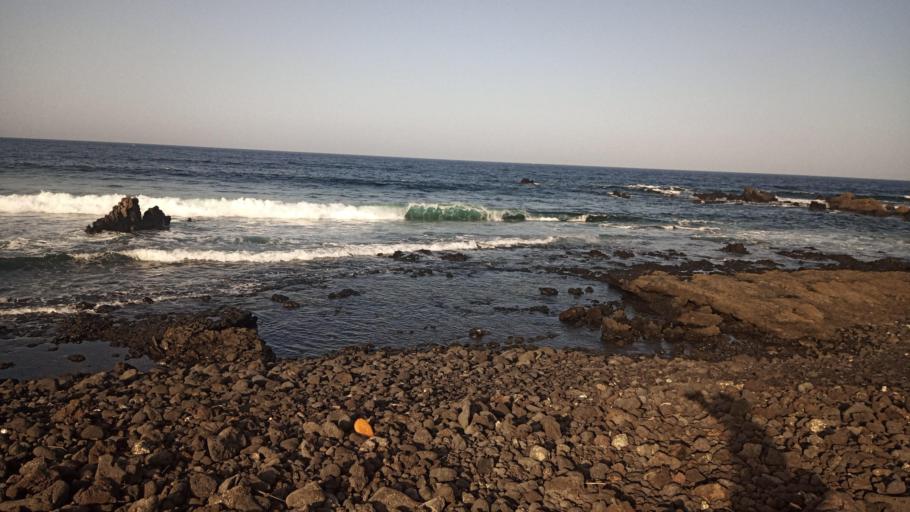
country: ES
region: Canary Islands
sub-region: Provincia de Las Palmas
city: Haria
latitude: 29.2086
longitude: -13.4260
